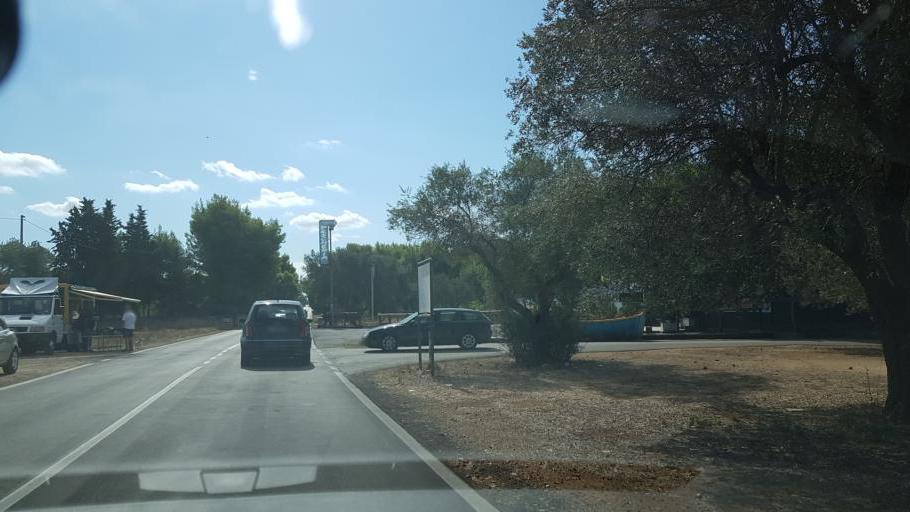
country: IT
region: Apulia
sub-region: Provincia di Lecce
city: Porto Cesareo
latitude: 40.2436
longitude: 17.9144
